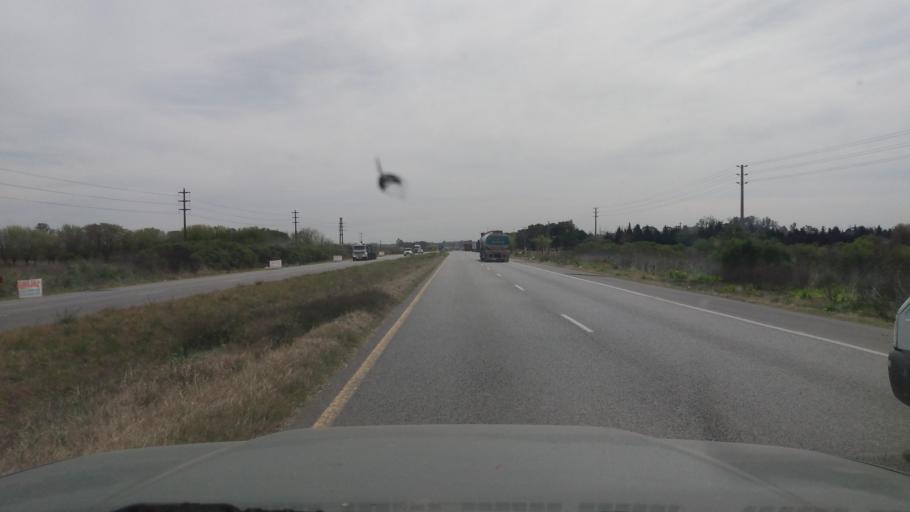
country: AR
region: Buenos Aires
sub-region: Partido de Lujan
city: Lujan
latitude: -34.5406
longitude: -59.0369
